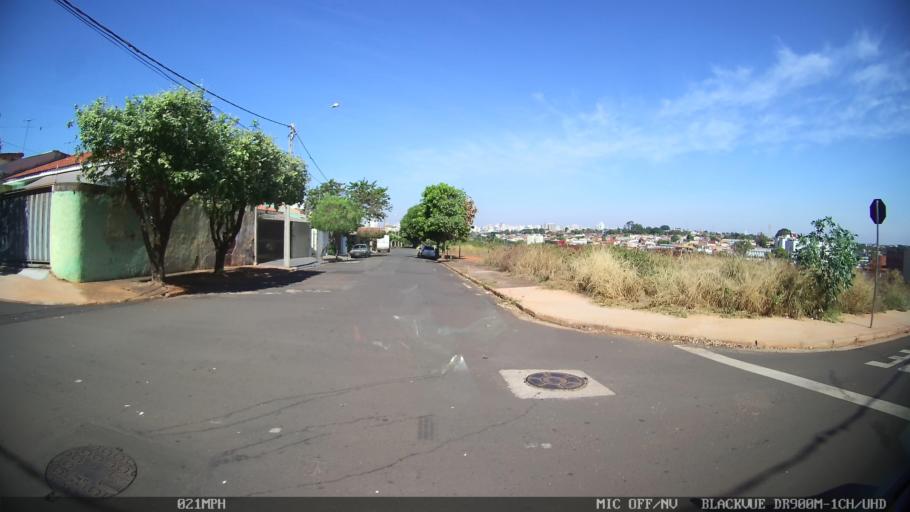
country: BR
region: Sao Paulo
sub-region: Sao Jose Do Rio Preto
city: Sao Jose do Rio Preto
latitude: -20.7823
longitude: -49.3765
